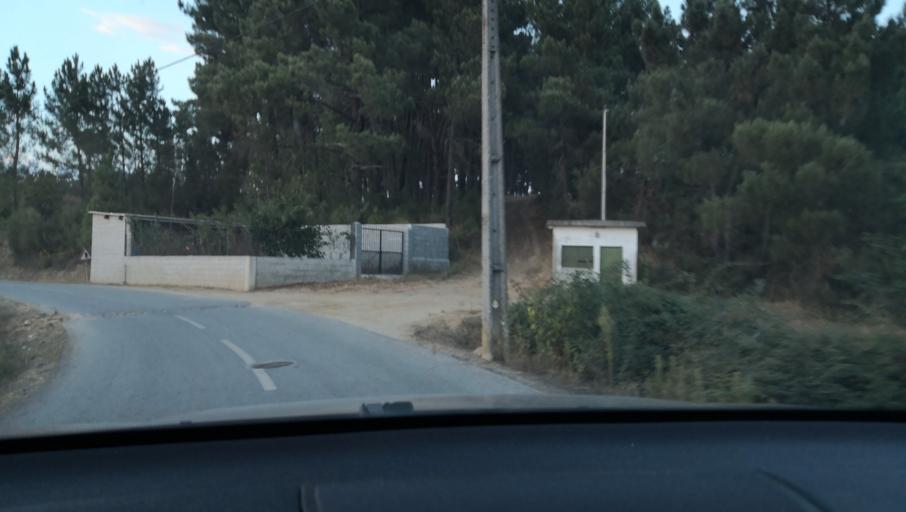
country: PT
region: Vila Real
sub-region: Sabrosa
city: Vilela
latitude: 41.2389
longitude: -7.6129
